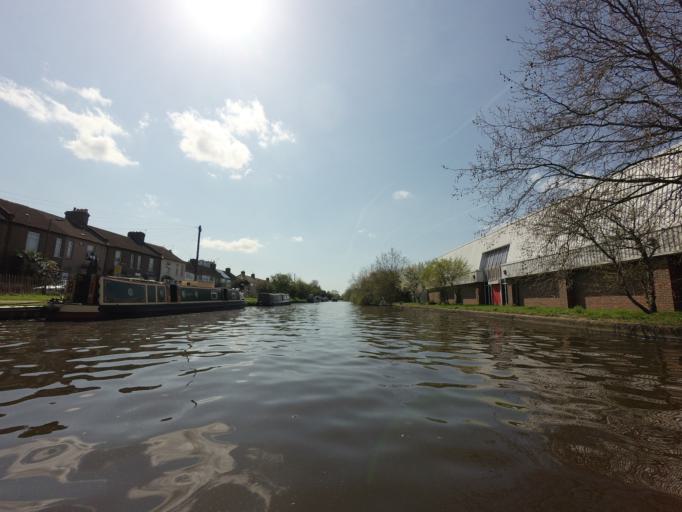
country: GB
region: England
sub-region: Greater London
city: Southall
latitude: 51.5122
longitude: -0.3909
